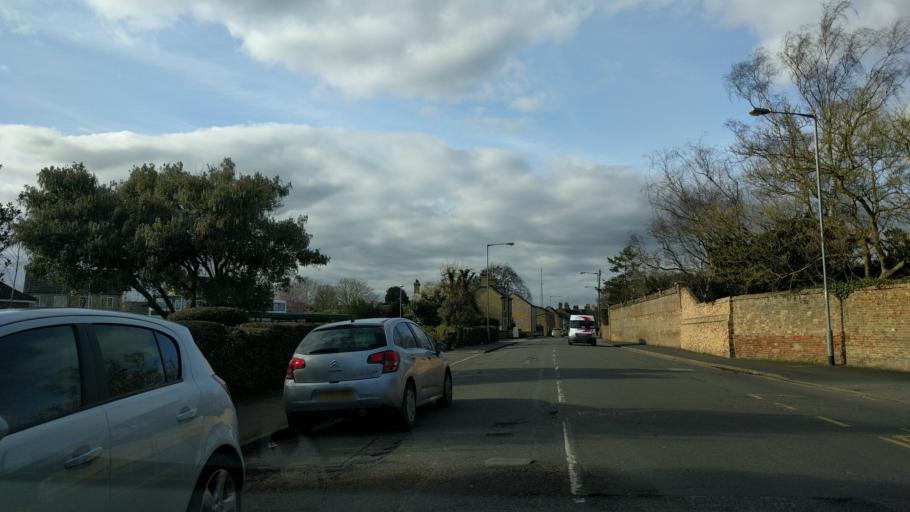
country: GB
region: England
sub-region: Cambridgeshire
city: Chatteris
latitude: 52.4505
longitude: 0.0529
